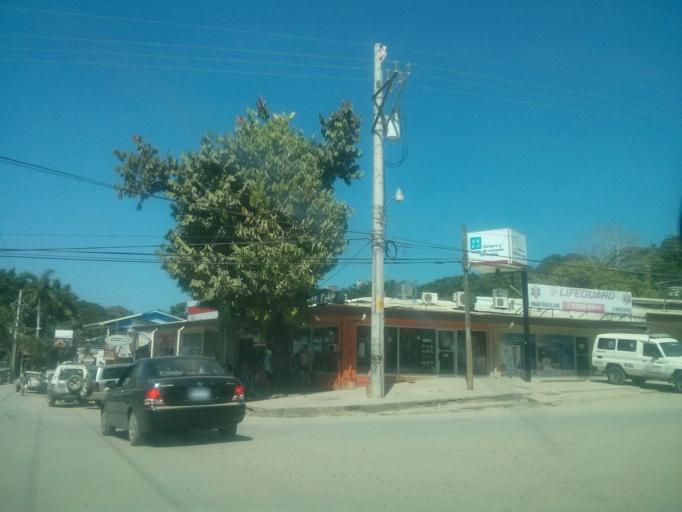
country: CR
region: Guanacaste
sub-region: Canton de Nandayure
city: Bejuco
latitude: 9.6279
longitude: -85.1502
